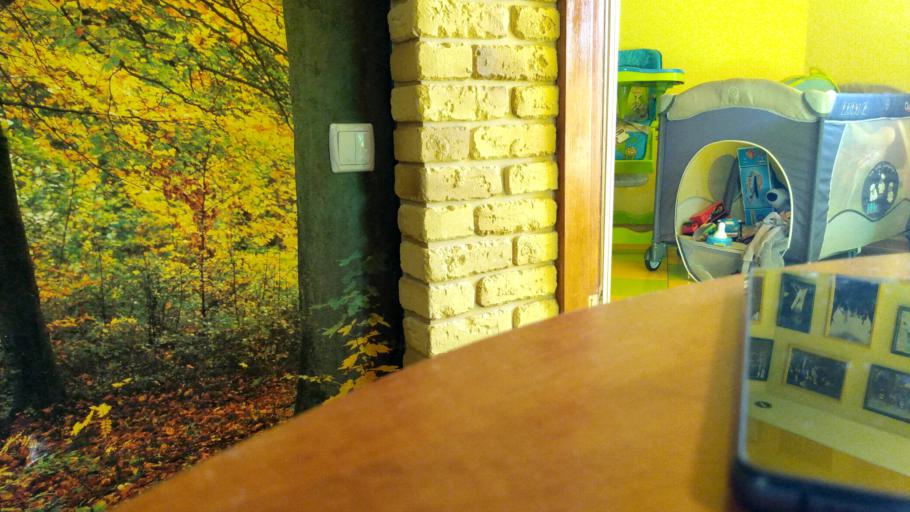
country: RU
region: Tverskaya
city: Likhoslavl'
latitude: 57.2409
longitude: 35.4449
